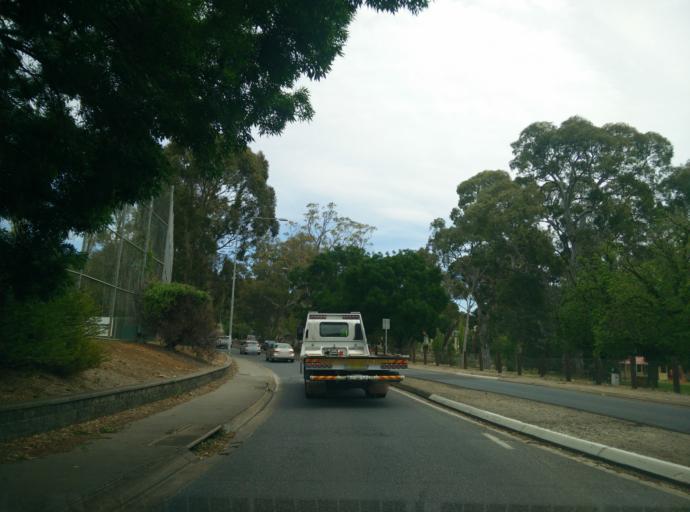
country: AU
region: South Australia
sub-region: Mitcham
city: Mitcham
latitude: -34.9800
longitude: 138.6226
